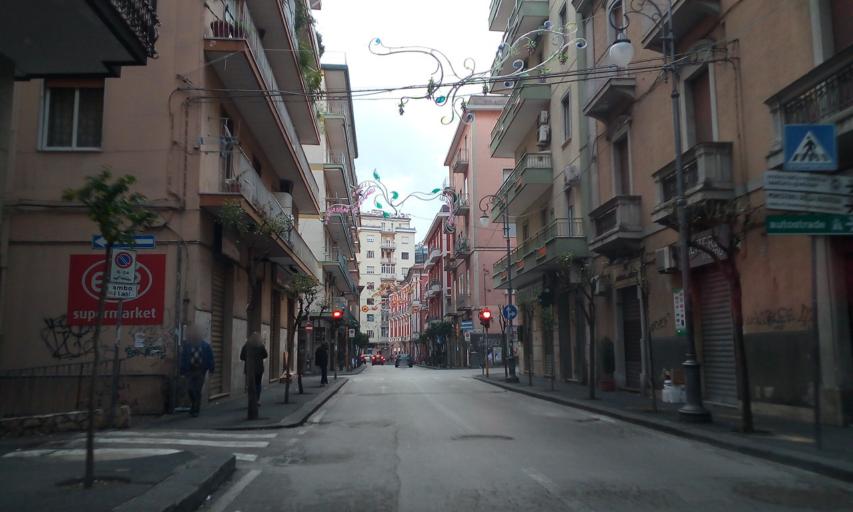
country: IT
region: Campania
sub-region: Provincia di Salerno
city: Capezzano Inferiore
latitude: 40.6828
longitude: 14.7687
